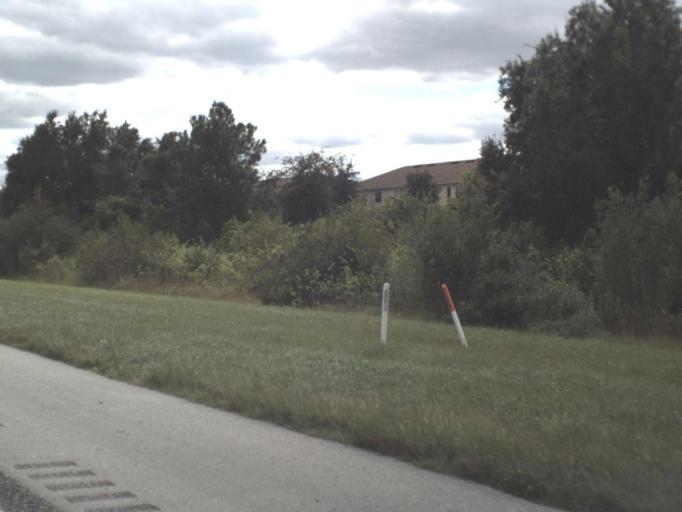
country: US
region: Florida
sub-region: Osceola County
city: Buenaventura Lakes
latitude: 28.2823
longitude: -81.3392
